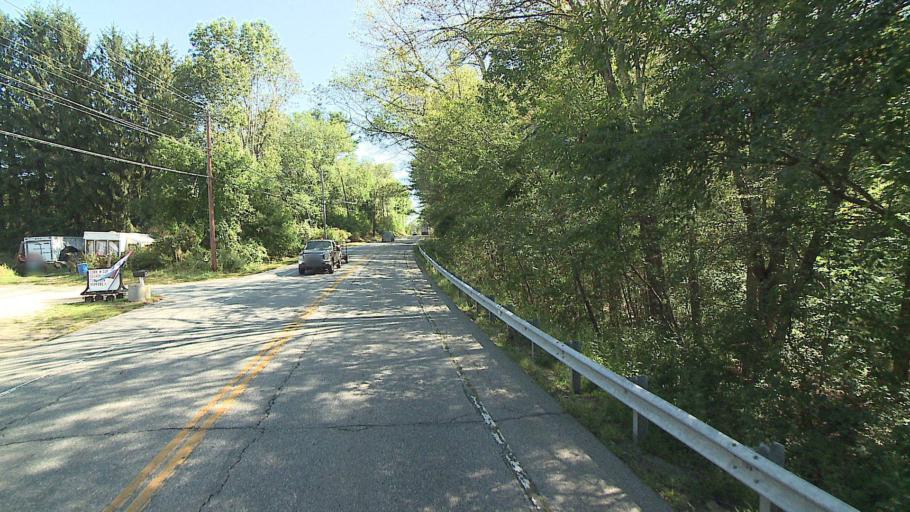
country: US
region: Connecticut
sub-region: New London County
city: Jewett City
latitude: 41.6332
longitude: -71.9603
